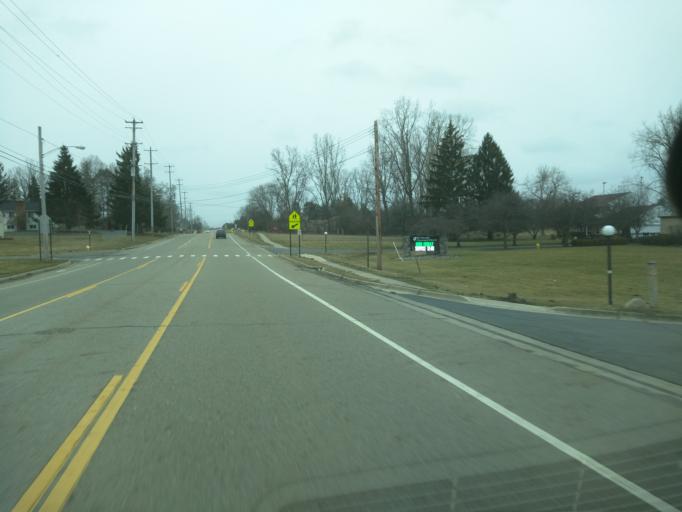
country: US
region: Michigan
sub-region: Eaton County
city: Waverly
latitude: 42.7519
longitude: -84.6225
